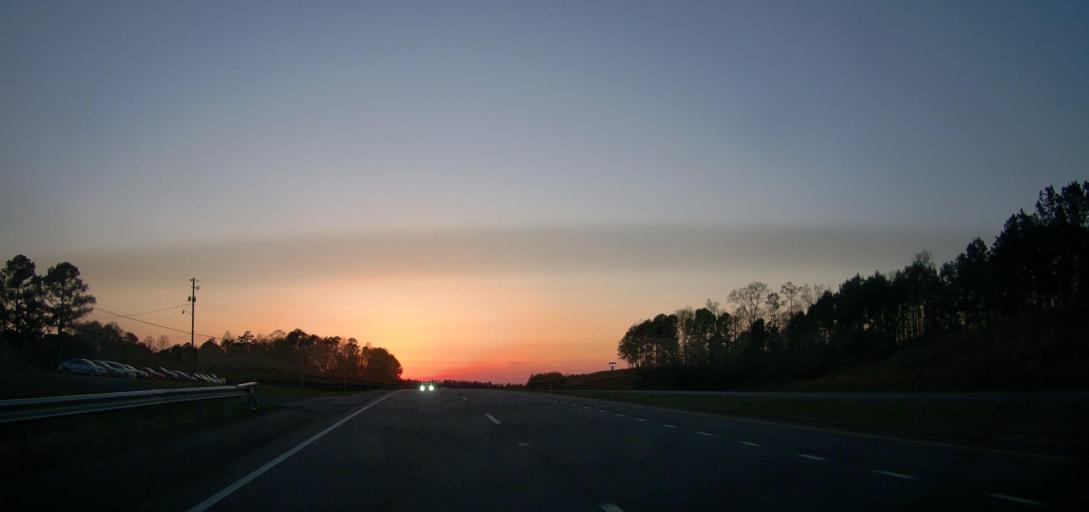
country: US
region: Alabama
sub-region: Tallapoosa County
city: Alexander City
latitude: 32.8854
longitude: -85.8641
